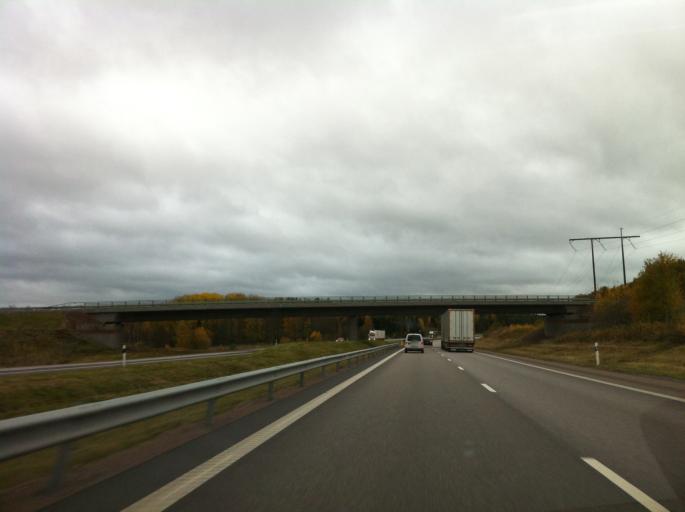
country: SE
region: OEstergoetland
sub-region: Vadstena Kommun
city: Herrestad
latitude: 58.2734
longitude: 14.8638
